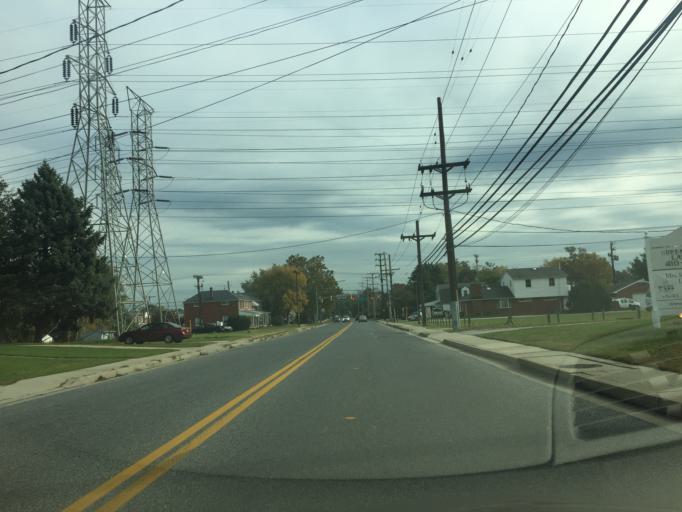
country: US
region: Maryland
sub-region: Baltimore County
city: Dundalk
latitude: 39.2710
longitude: -76.5007
